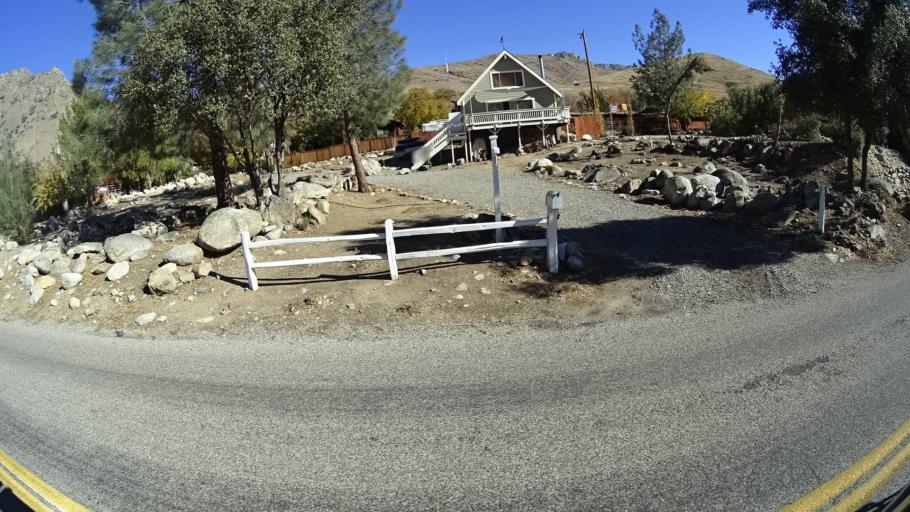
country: US
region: California
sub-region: Kern County
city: Kernville
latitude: 35.7903
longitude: -118.4479
